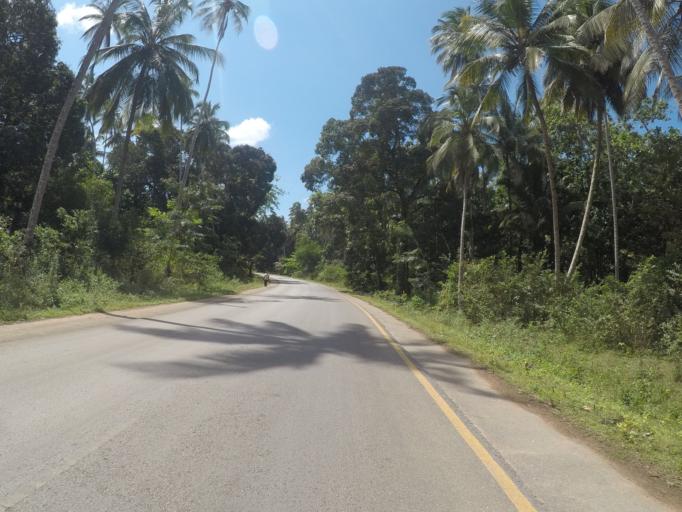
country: TZ
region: Zanzibar Central/South
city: Koani
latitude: -6.1483
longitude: 39.3293
